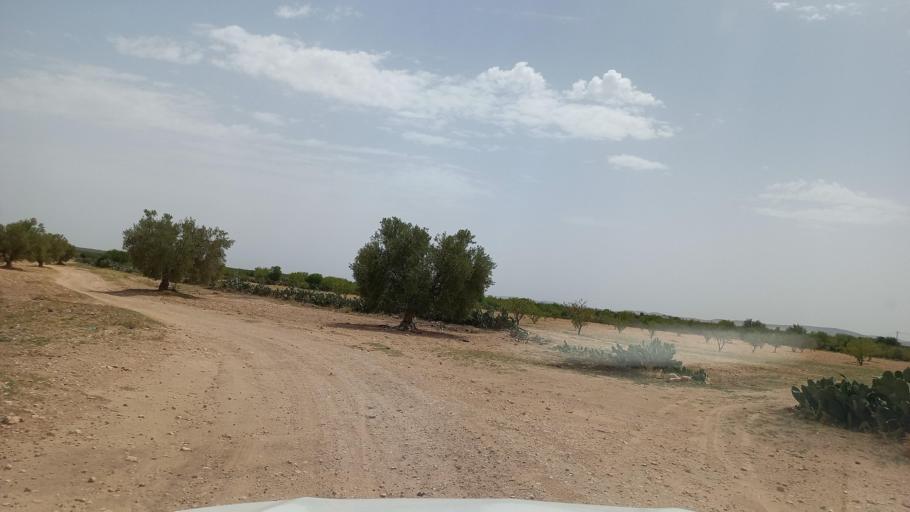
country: TN
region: Al Qasrayn
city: Kasserine
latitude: 35.2909
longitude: 9.0207
